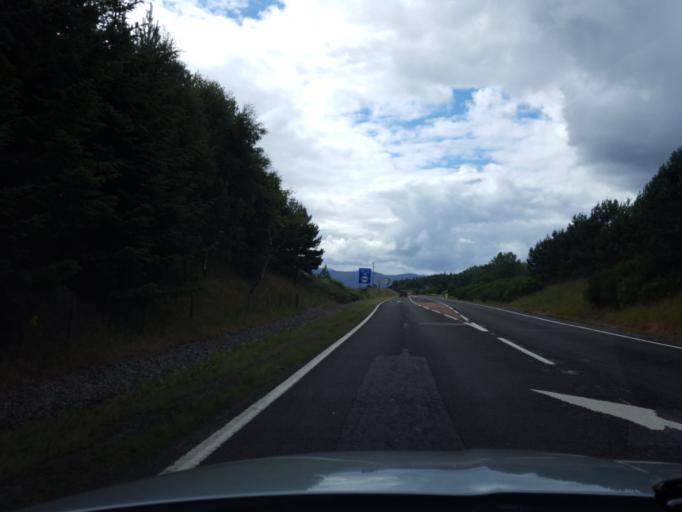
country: GB
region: Scotland
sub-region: Highland
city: Grantown on Spey
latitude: 57.2999
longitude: -3.6612
